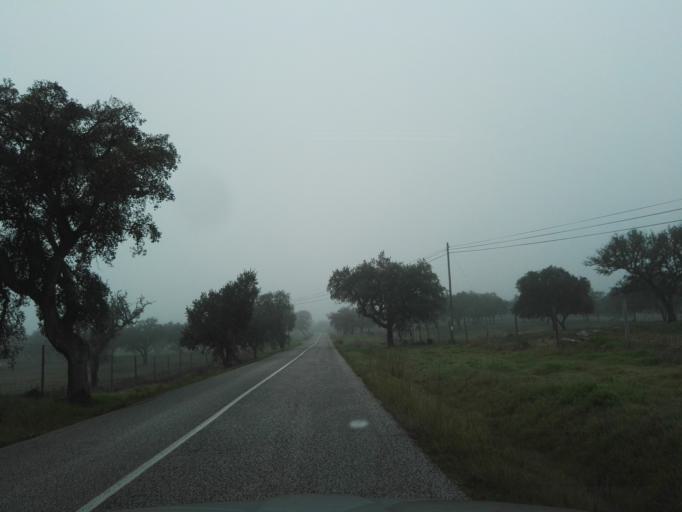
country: PT
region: Evora
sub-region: Montemor-O-Novo
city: Montemor-o-Novo
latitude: 38.7746
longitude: -8.2052
